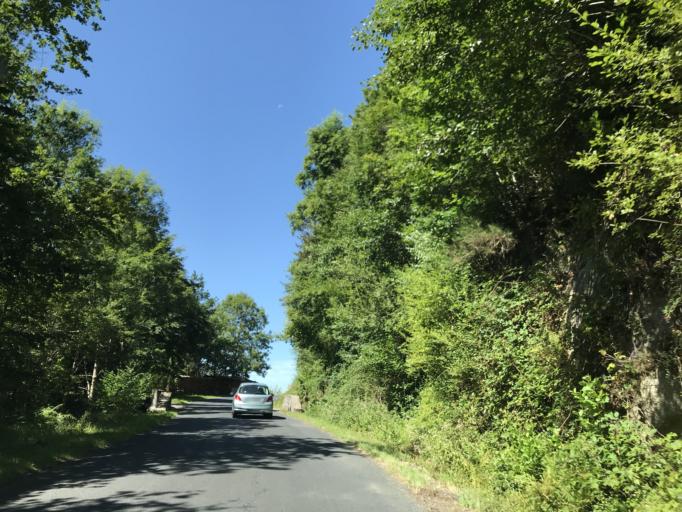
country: FR
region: Auvergne
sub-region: Departement du Puy-de-Dome
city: Job
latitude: 45.6603
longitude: 3.7188
